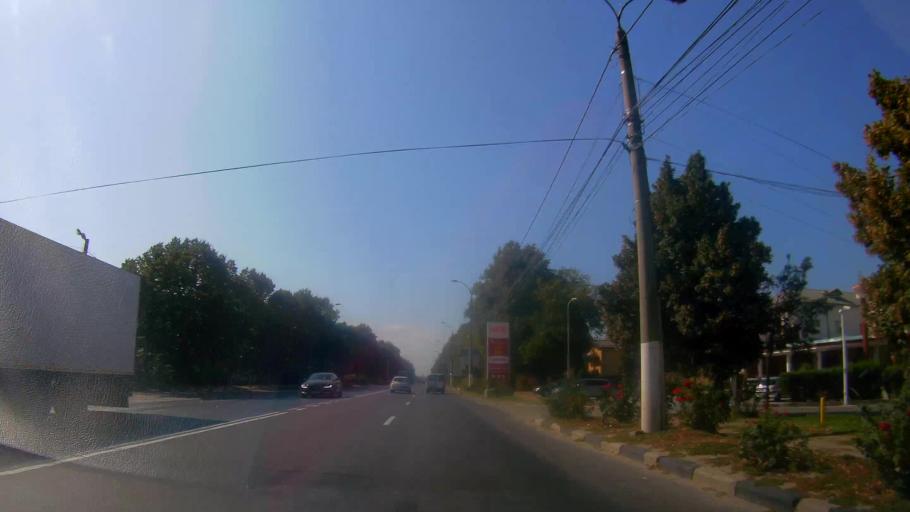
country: RO
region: Giurgiu
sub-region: Comuna Fratesti
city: Remus
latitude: 43.9281
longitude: 25.9751
